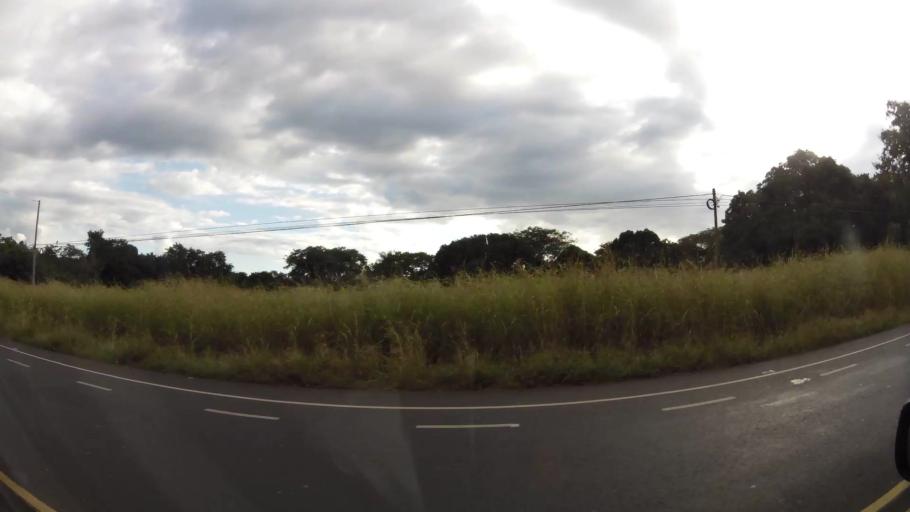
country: CR
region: Puntarenas
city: Esparza
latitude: 9.8931
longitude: -84.6500
